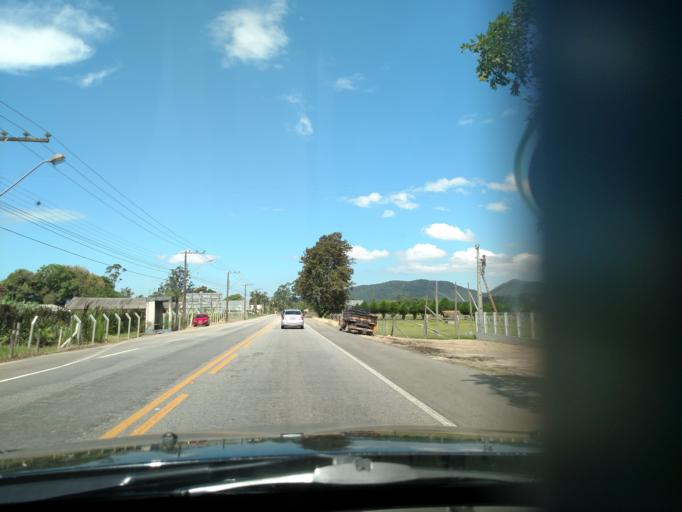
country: BR
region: Santa Catarina
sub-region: Itajai
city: Itajai
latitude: -26.8741
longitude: -48.7860
